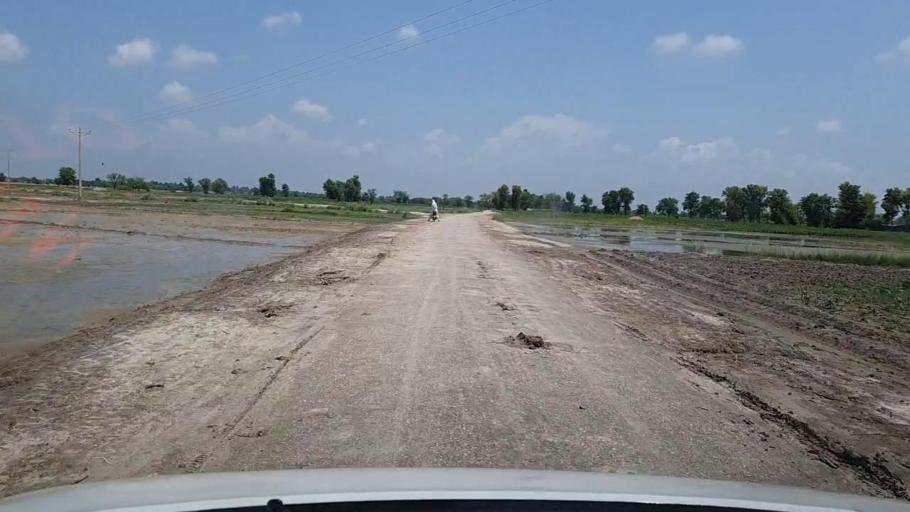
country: PK
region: Sindh
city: Kandiaro
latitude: 26.9871
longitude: 68.2263
